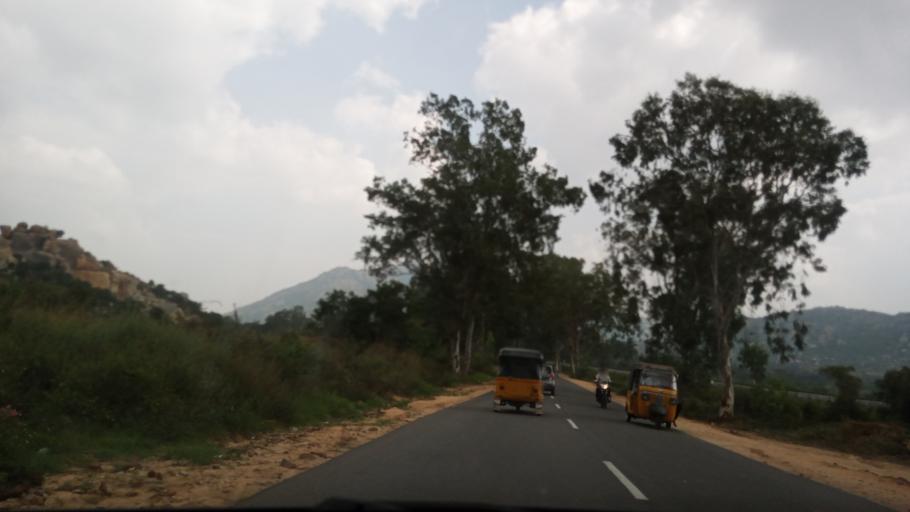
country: IN
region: Andhra Pradesh
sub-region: Chittoor
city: Madanapalle
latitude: 13.6382
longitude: 78.5765
